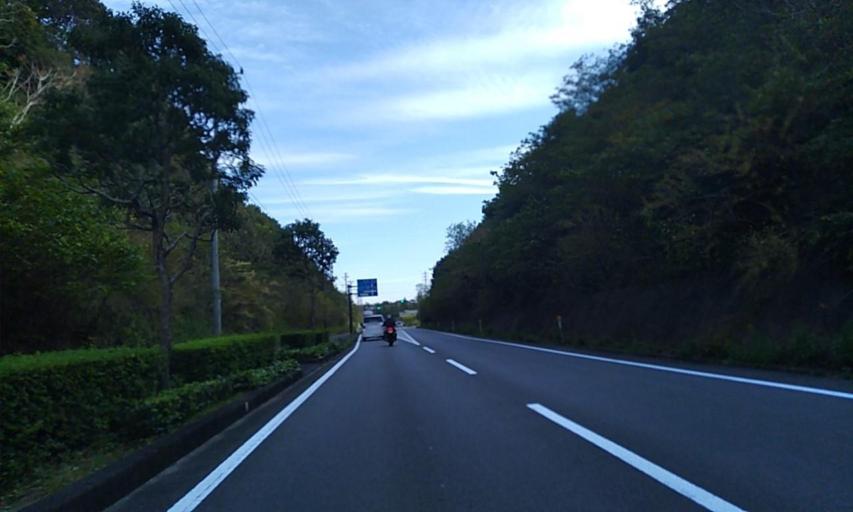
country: JP
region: Mie
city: Toba
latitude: 34.3556
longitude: 136.8063
